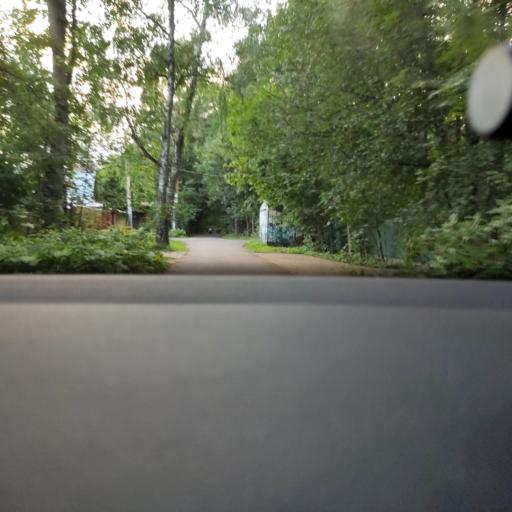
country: RU
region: Moscow
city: Novo-Peredelkino
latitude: 55.6500
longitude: 37.3193
